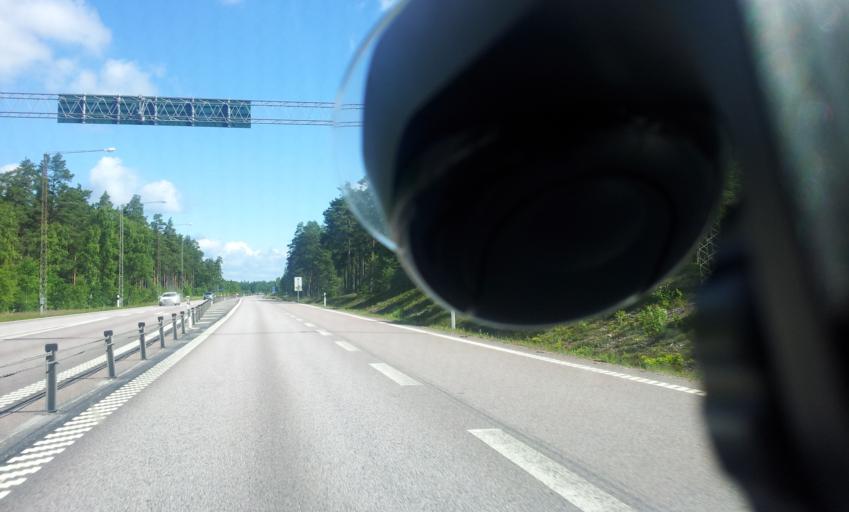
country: SE
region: Kalmar
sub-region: Monsteras Kommun
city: Moensteras
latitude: 57.0815
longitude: 16.4836
